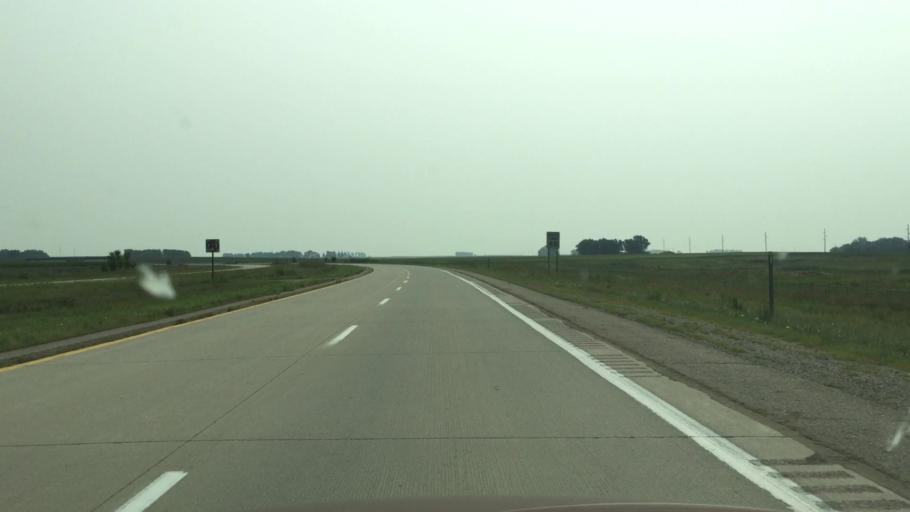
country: US
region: Iowa
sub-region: Osceola County
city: Sibley
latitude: 43.3843
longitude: -95.7338
